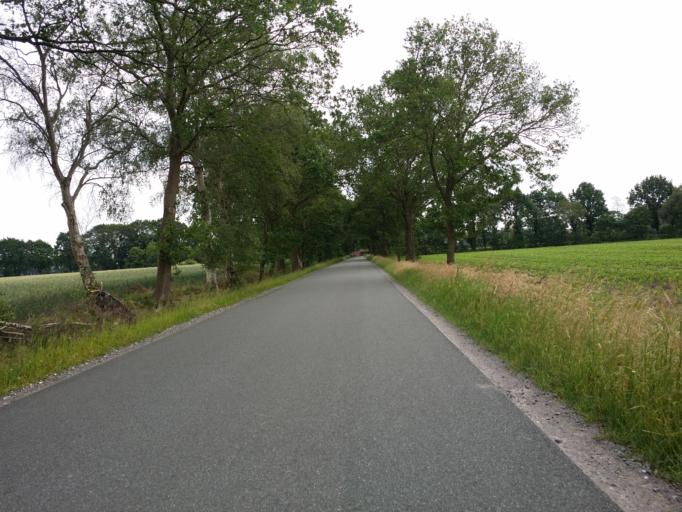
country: DE
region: Lower Saxony
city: Bockhorn
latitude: 53.3502
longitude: 8.0224
